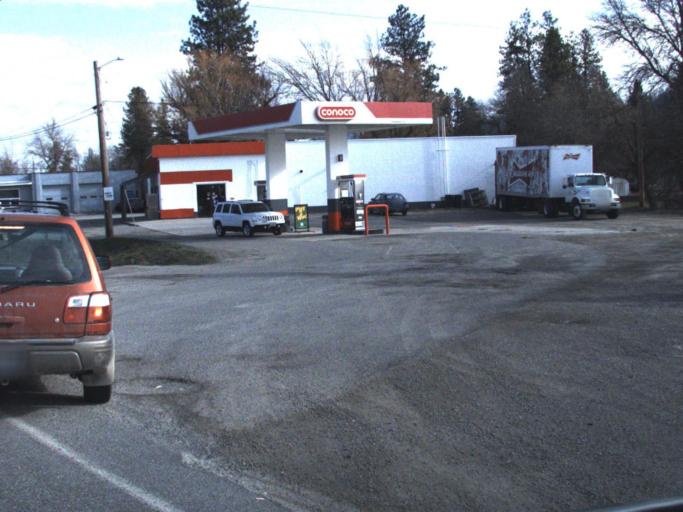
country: US
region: Washington
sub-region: Pend Oreille County
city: Newport
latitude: 48.3365
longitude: -117.3043
